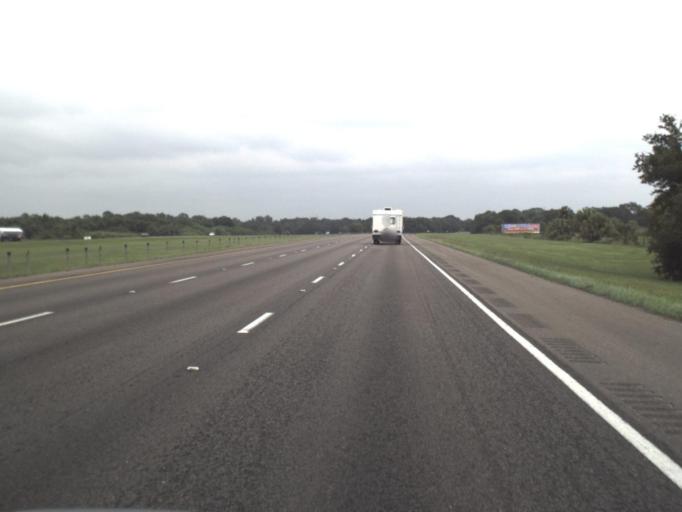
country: US
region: Florida
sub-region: Hillsborough County
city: Ruskin
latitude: 27.6354
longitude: -82.4663
